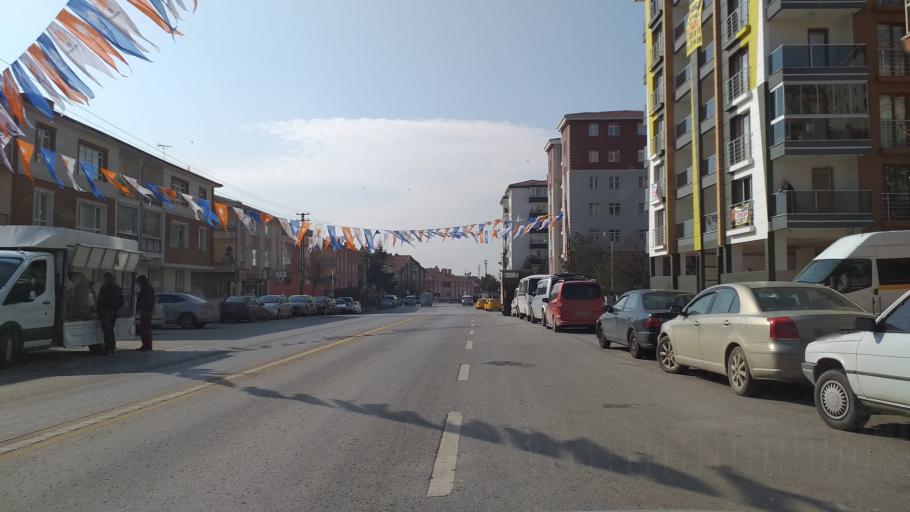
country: TR
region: Ankara
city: Ankara
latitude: 39.9908
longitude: 32.8559
